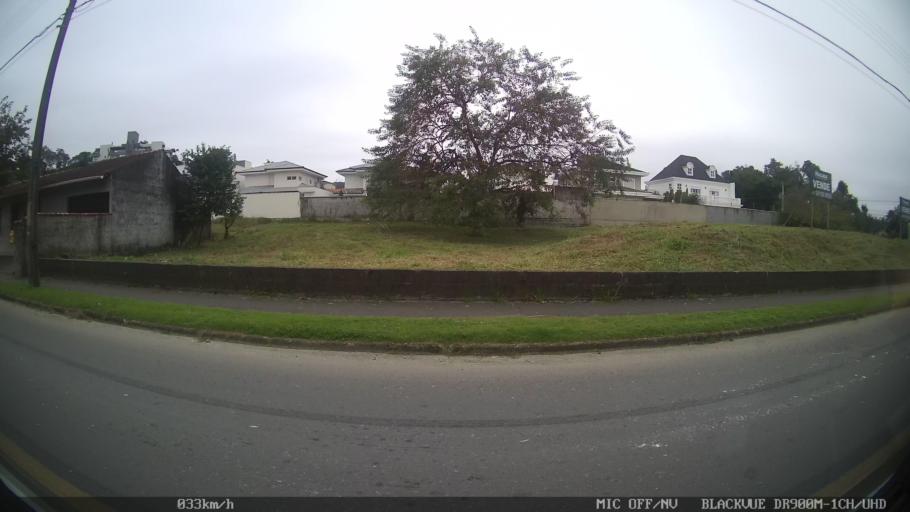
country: BR
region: Santa Catarina
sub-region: Joinville
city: Joinville
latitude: -26.2748
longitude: -48.8414
